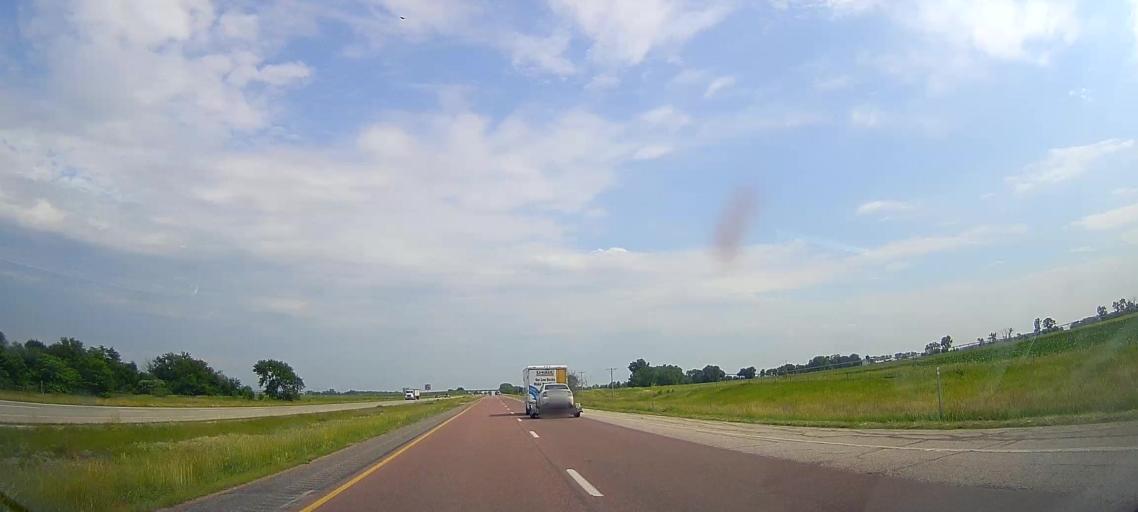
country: US
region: Iowa
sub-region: Monona County
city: Onawa
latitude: 41.9882
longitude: -96.1085
